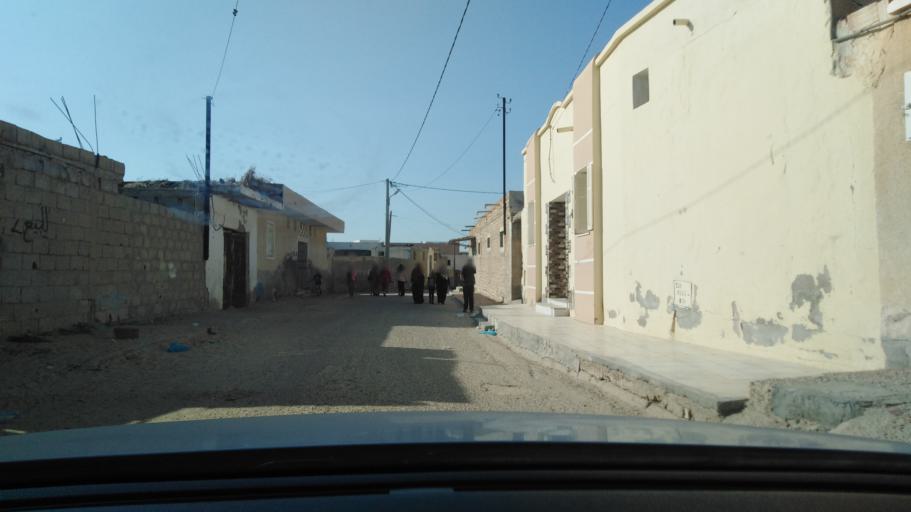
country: TN
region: Qabis
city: Gabes
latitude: 33.9368
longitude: 10.0700
